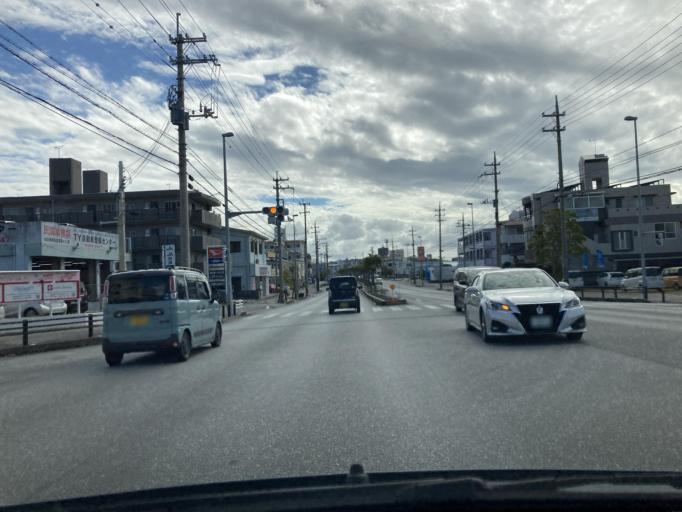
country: JP
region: Okinawa
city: Tomigusuku
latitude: 26.1606
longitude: 127.7227
